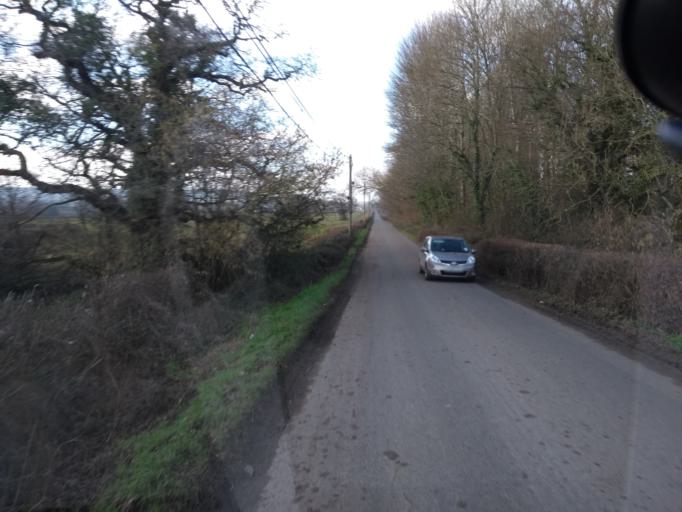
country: GB
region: England
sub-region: Somerset
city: Creech Saint Michael
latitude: 50.9630
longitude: -3.0265
